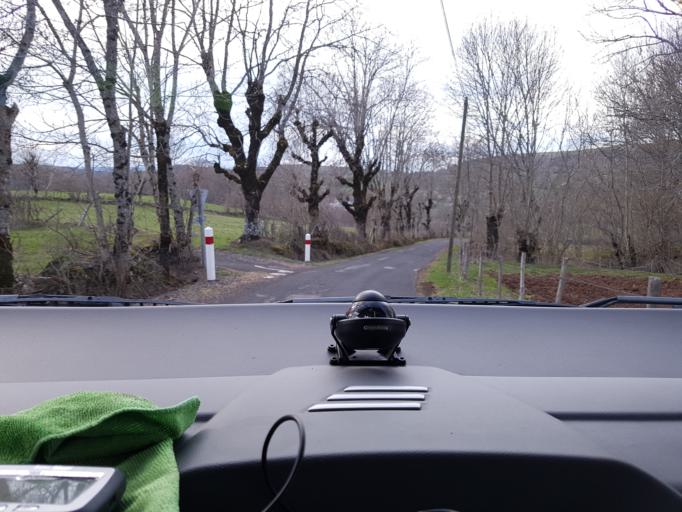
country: FR
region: Midi-Pyrenees
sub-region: Departement de l'Aveyron
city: Laguiole
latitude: 44.6482
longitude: 2.8761
